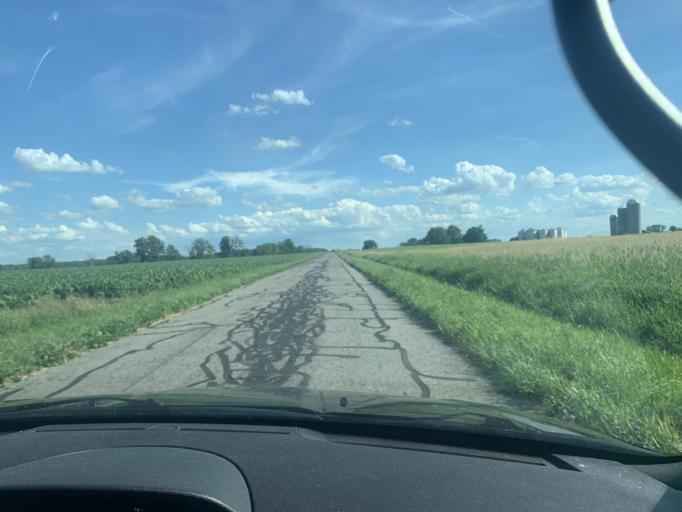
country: US
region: Ohio
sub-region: Logan County
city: De Graff
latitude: 40.3288
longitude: -83.8728
